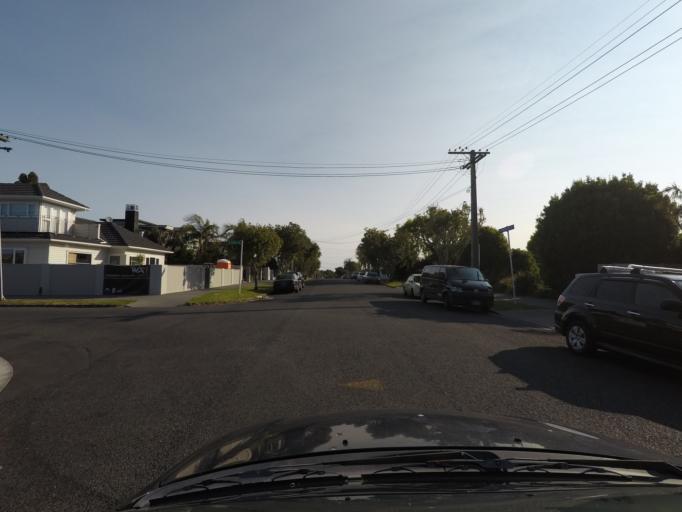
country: NZ
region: Auckland
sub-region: Auckland
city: Rosebank
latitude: -36.8574
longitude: 174.7015
